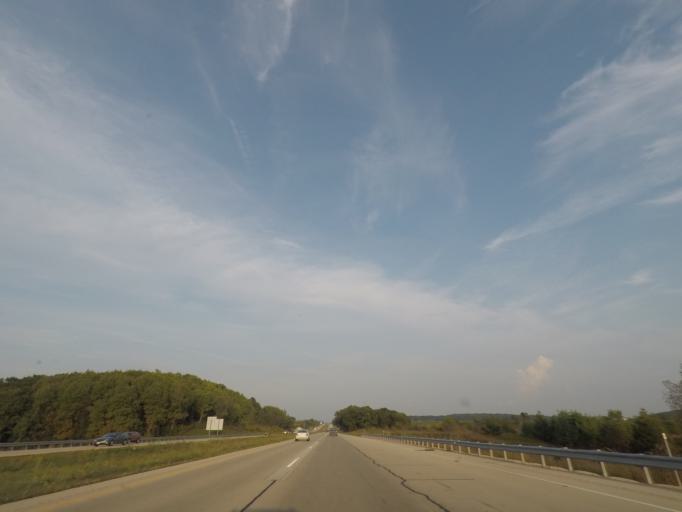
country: US
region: Wisconsin
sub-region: Dane County
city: Deerfield
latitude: 43.1091
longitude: -89.0770
